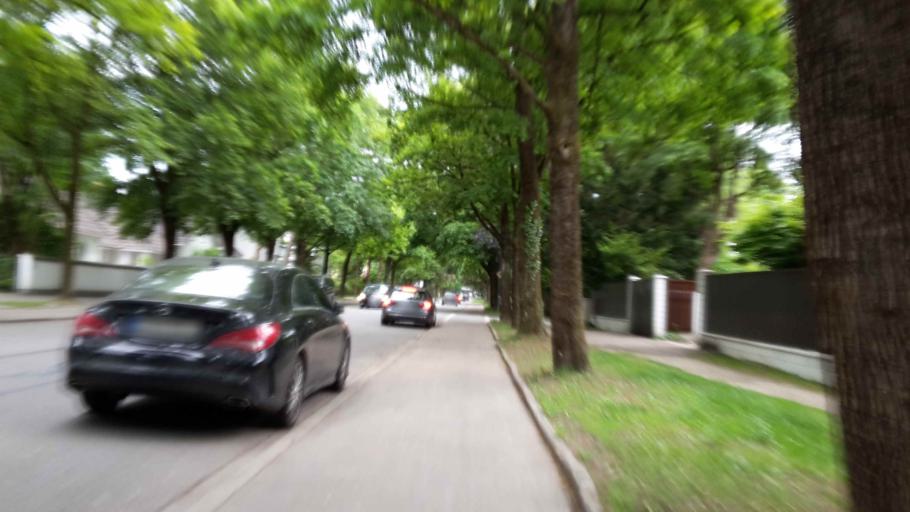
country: DE
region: Bavaria
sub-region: Upper Bavaria
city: Bogenhausen
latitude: 48.1601
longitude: 11.6131
